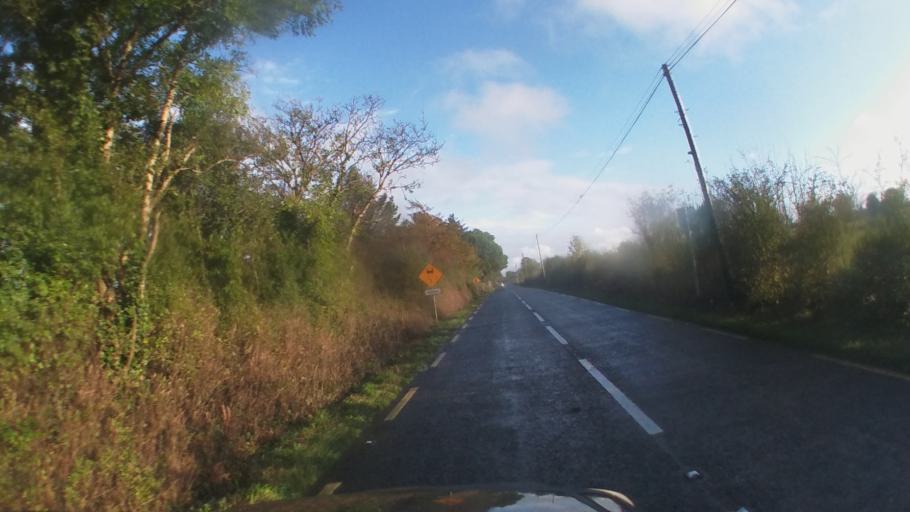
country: IE
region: Connaught
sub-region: Roscommon
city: Castlerea
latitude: 53.8551
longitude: -8.3939
